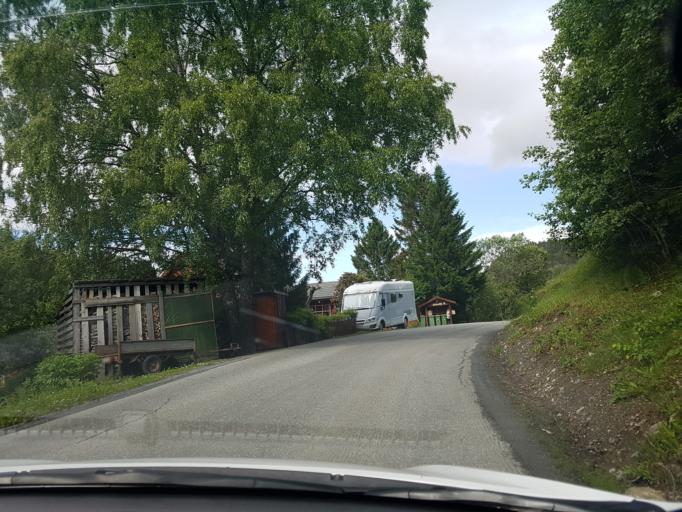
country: NO
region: Nord-Trondelag
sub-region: Stjordal
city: Stjordalshalsen
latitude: 63.5986
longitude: 10.9689
